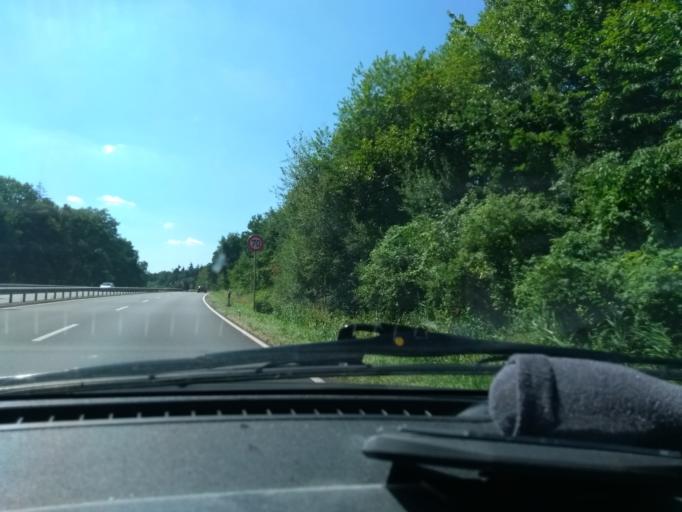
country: DE
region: Lower Saxony
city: Meppen
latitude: 52.6779
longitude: 7.3037
